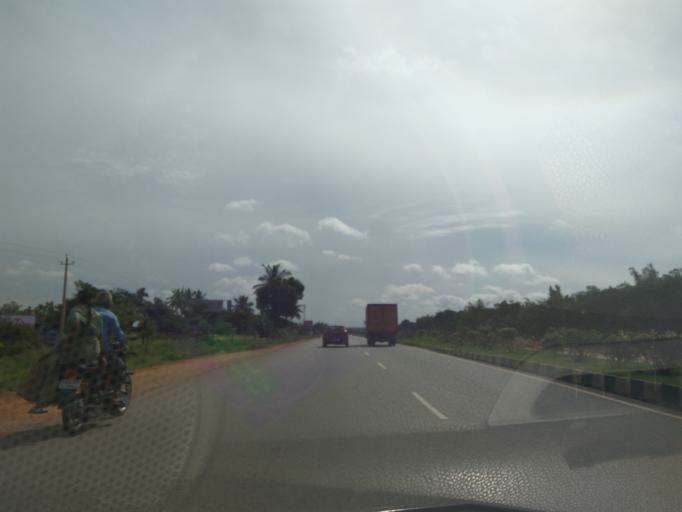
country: IN
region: Karnataka
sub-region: Bangalore Rural
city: Dasarahalli
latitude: 13.0956
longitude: 77.8489
